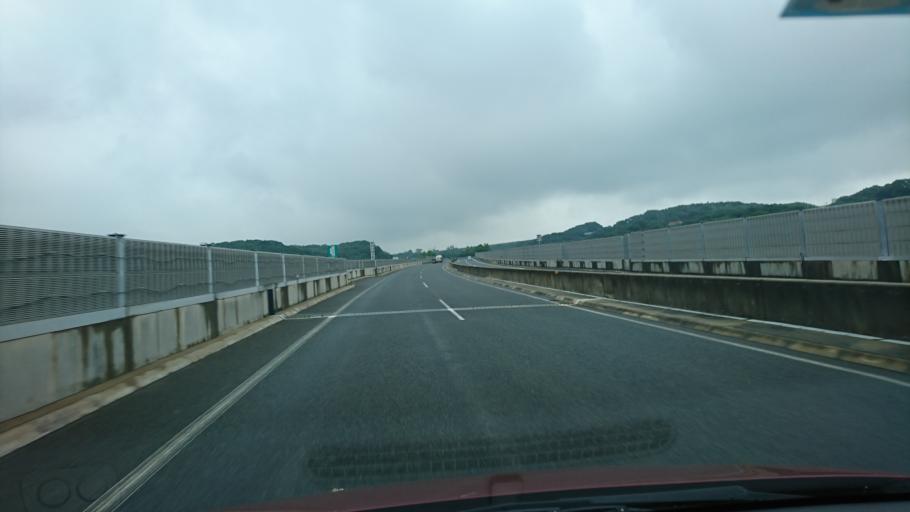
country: JP
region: Hyogo
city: Akashi
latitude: 34.6771
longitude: 135.0350
